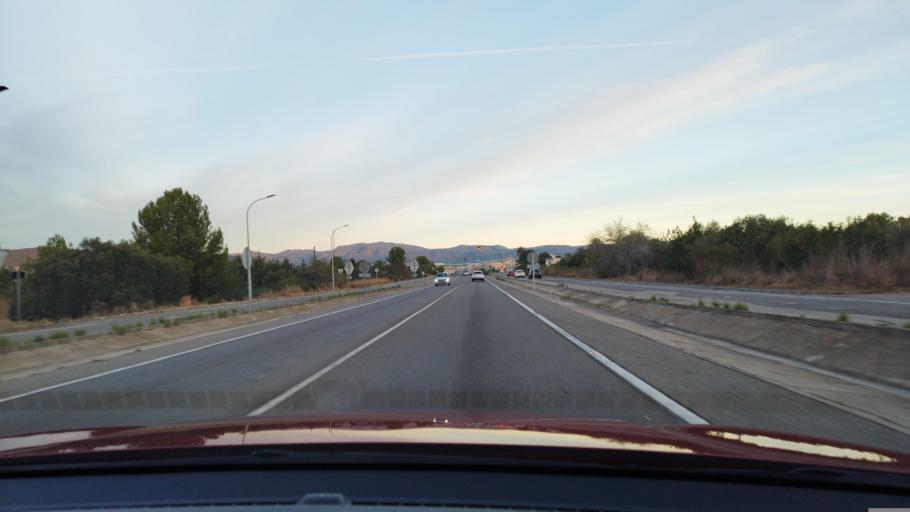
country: ES
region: Catalonia
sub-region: Provincia de Tarragona
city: El Vendrell
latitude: 41.2117
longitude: 1.5477
